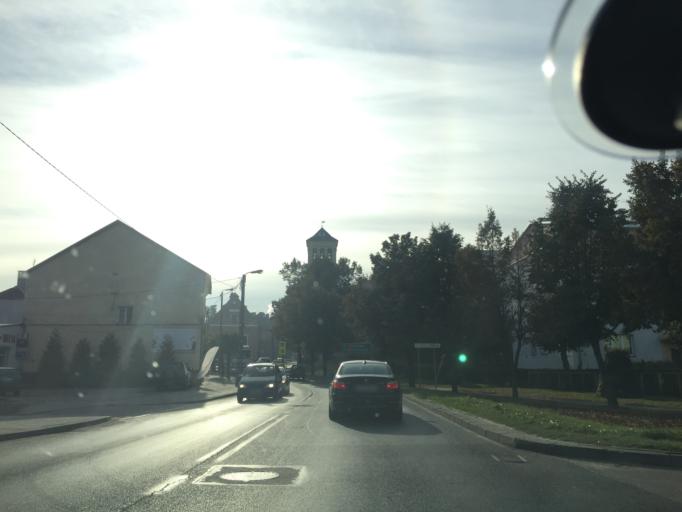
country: PL
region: Warmian-Masurian Voivodeship
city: Dobre Miasto
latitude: 53.9868
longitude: 20.4004
